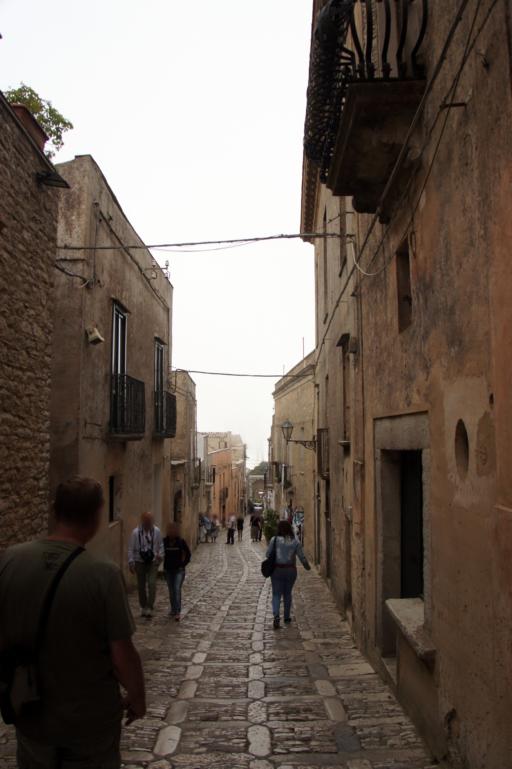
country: IT
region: Sicily
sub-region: Trapani
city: Erice
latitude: 38.0367
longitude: 12.5852
